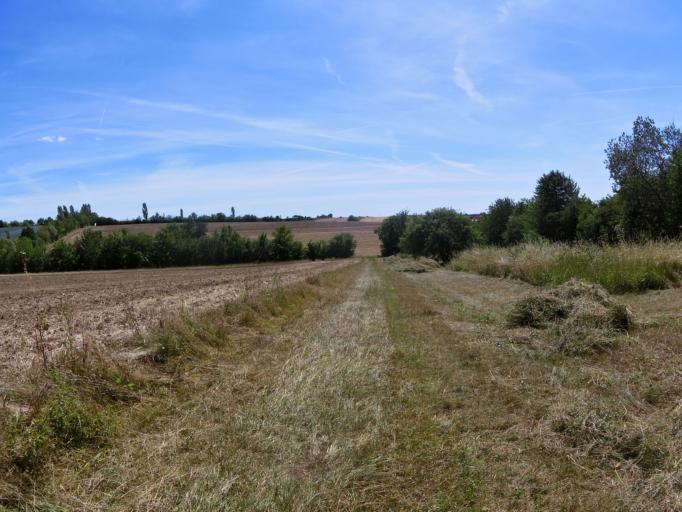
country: DE
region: Bavaria
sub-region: Regierungsbezirk Unterfranken
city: Hettstadt
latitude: 49.8081
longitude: 9.8279
